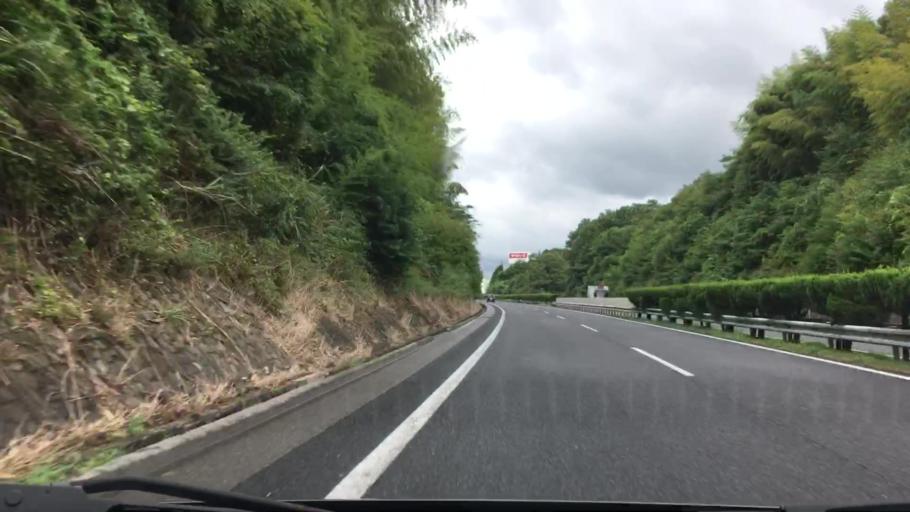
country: JP
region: Okayama
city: Tsuyama
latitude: 35.0446
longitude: 134.1123
